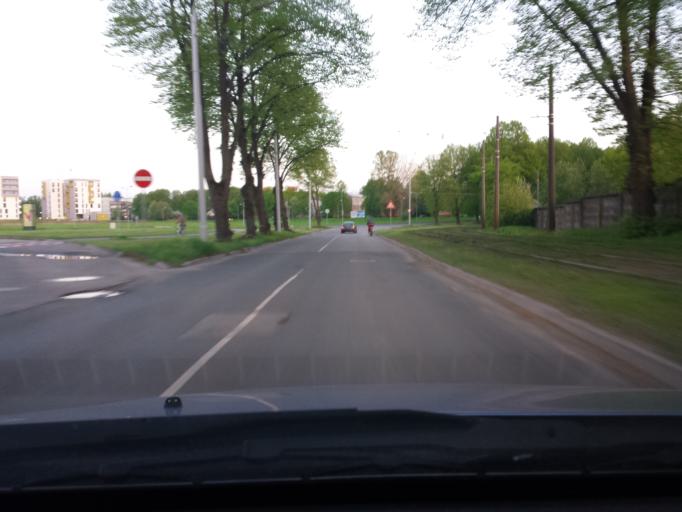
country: LV
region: Riga
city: Jaunciems
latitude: 56.9914
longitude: 24.1651
